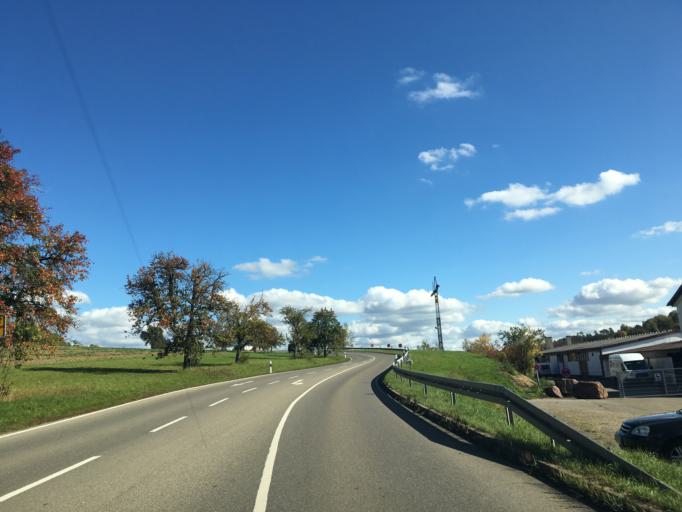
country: DE
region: Baden-Wuerttemberg
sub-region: Karlsruhe Region
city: Ostelsheim
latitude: 48.7271
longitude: 8.8548
